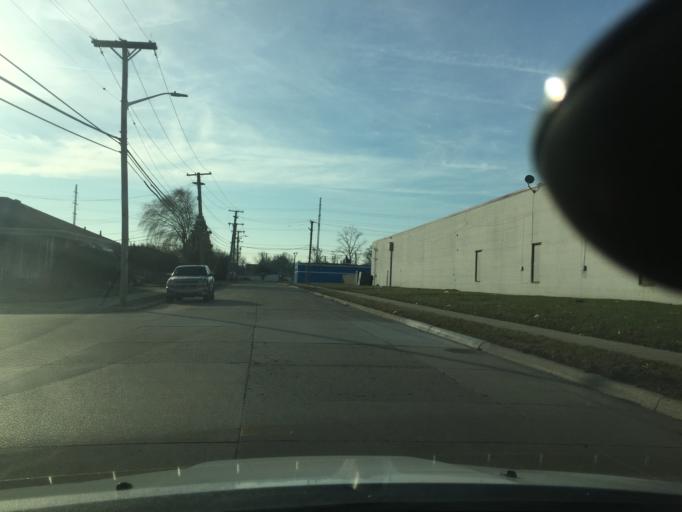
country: US
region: Michigan
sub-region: Macomb County
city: Eastpointe
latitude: 42.4518
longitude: -82.9635
